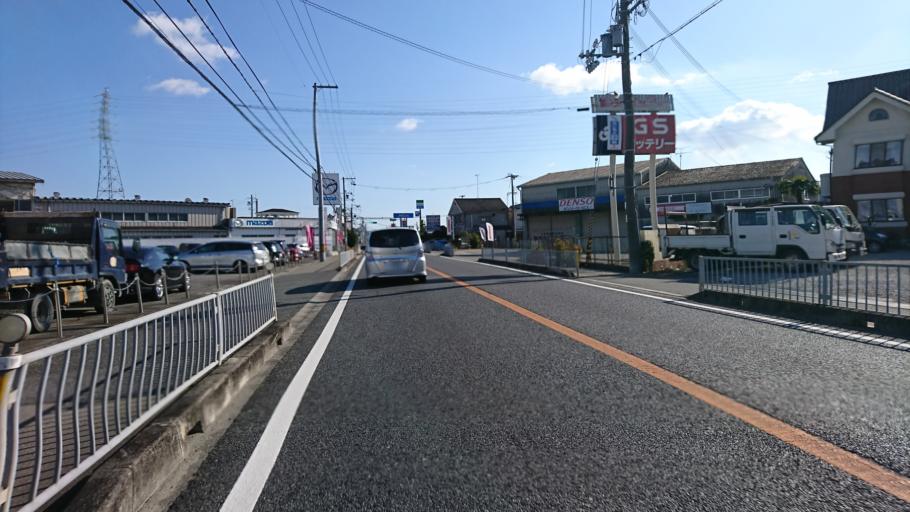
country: JP
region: Hyogo
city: Kakogawacho-honmachi
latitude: 34.7805
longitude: 134.8175
